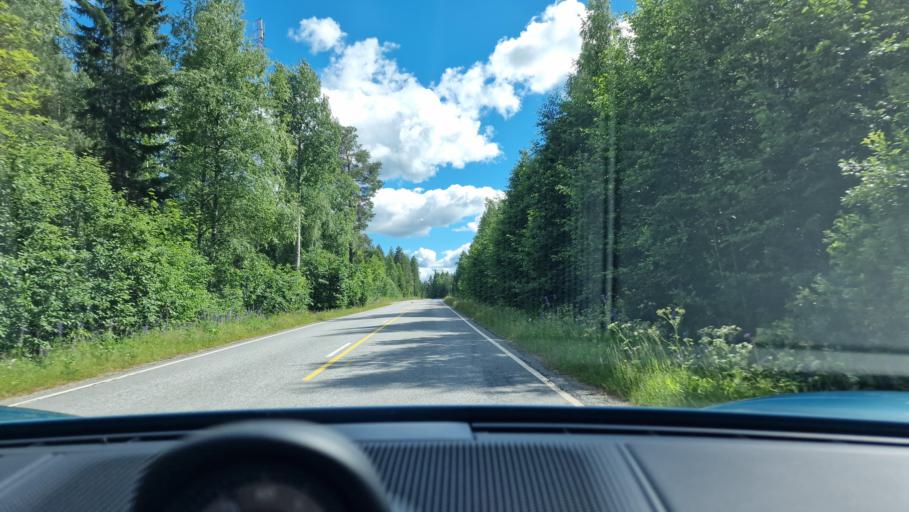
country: FI
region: Southern Ostrobothnia
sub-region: Jaerviseutu
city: Soini
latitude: 62.8216
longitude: 24.3468
